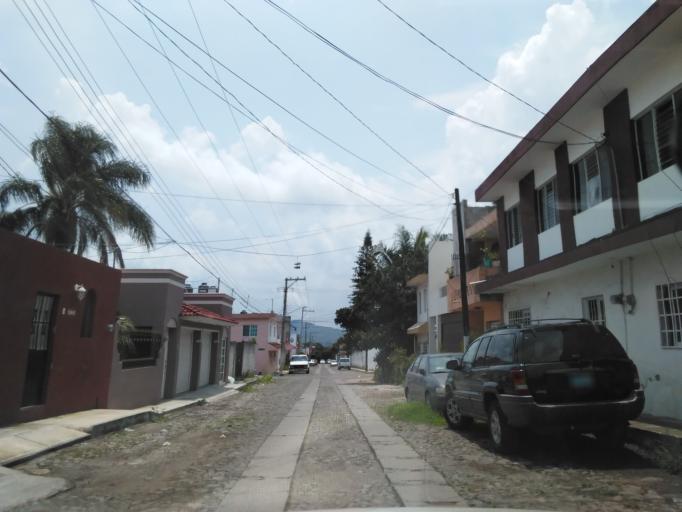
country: MX
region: Nayarit
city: Tepic
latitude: 21.5117
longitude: -104.9132
